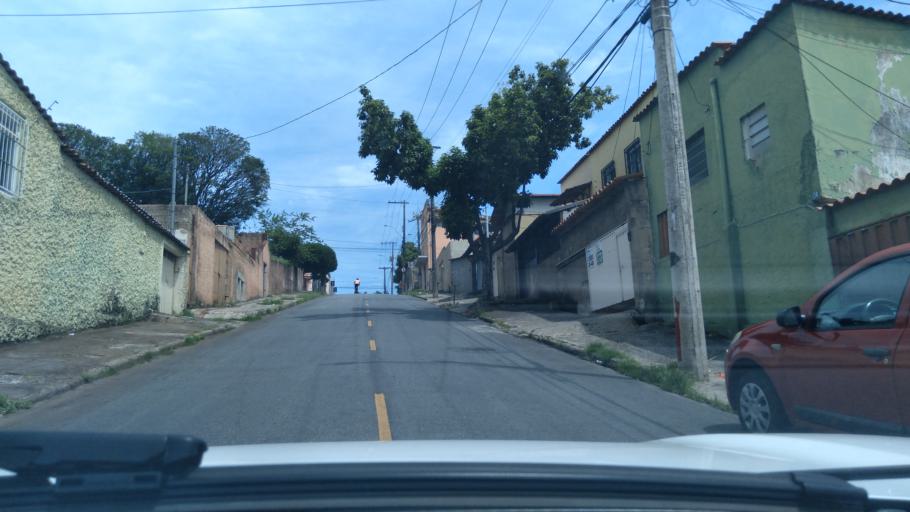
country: BR
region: Minas Gerais
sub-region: Contagem
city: Contagem
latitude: -19.9234
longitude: -44.0019
